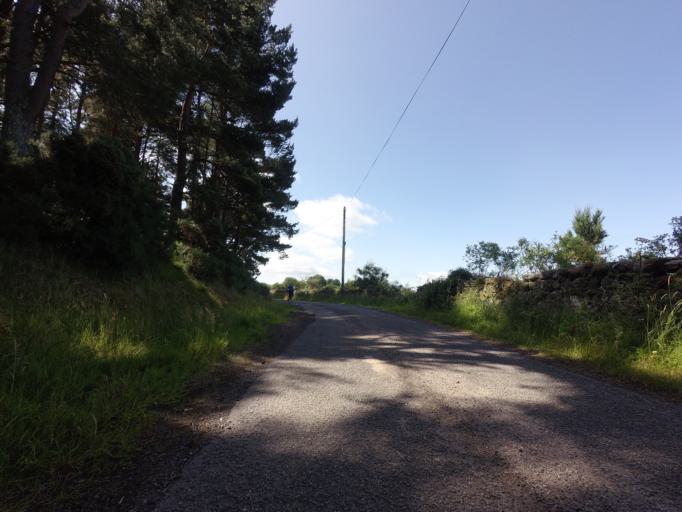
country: GB
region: Scotland
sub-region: Highland
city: Nairn
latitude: 57.5030
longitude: -3.9384
